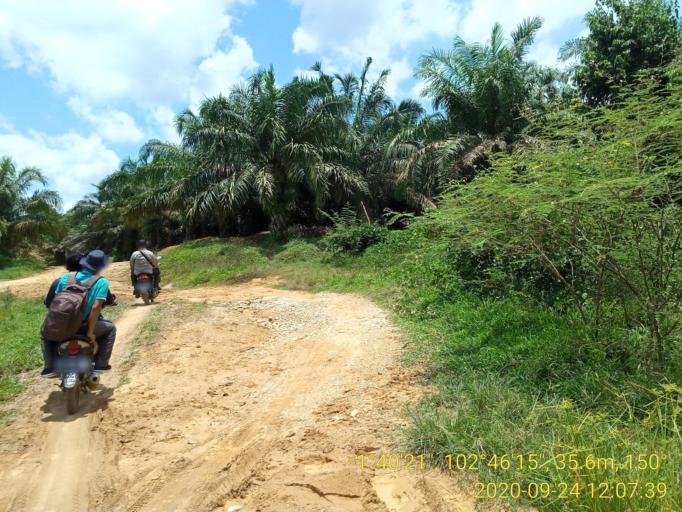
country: ID
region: Jambi
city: Sungaibengkal
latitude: -1.6728
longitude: 102.7711
